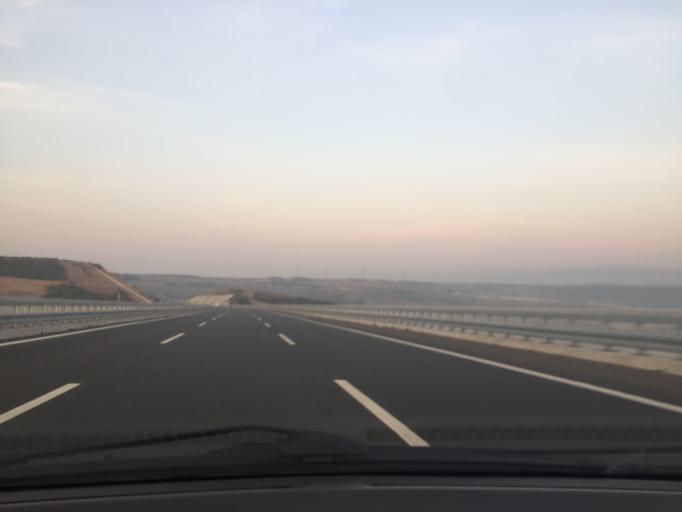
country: TR
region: Bursa
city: Mahmudiye
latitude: 40.2767
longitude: 28.5238
